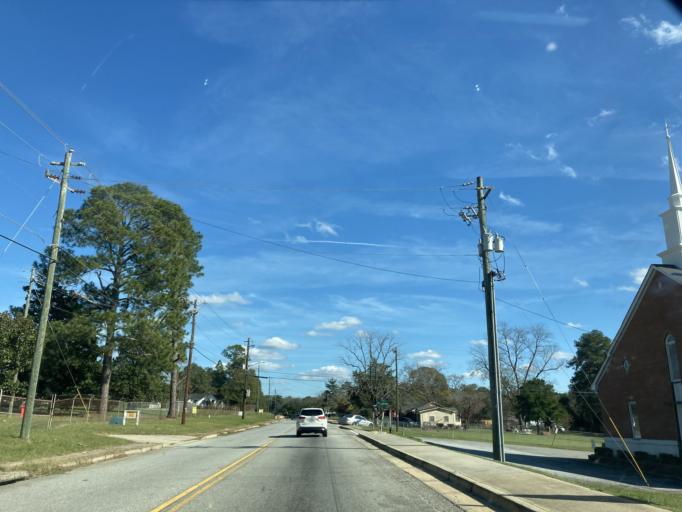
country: US
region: Georgia
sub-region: Bibb County
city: Macon
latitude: 32.8603
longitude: -83.5777
